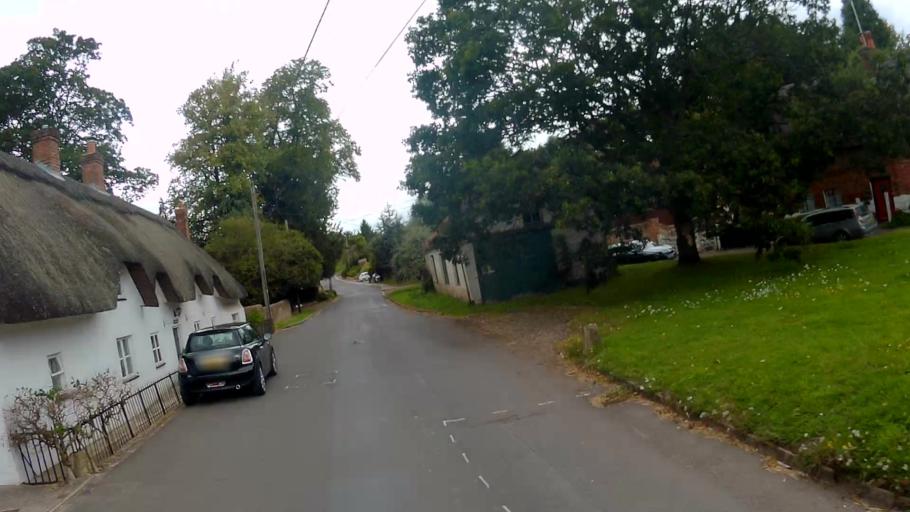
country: GB
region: England
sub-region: Hampshire
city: Overton
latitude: 51.2126
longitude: -1.1968
